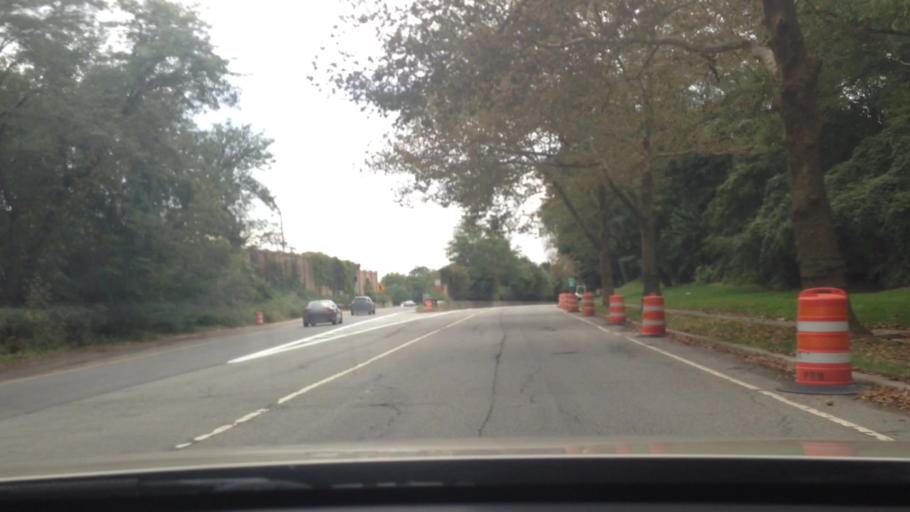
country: US
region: New York
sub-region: Nassau County
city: Jericho
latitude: 40.7828
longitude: -73.5586
